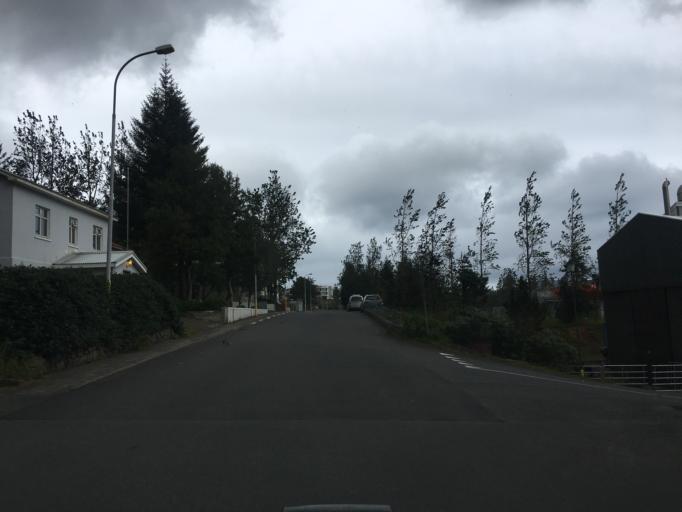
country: IS
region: East
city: Neskaupstadur
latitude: 65.1484
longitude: -13.6900
